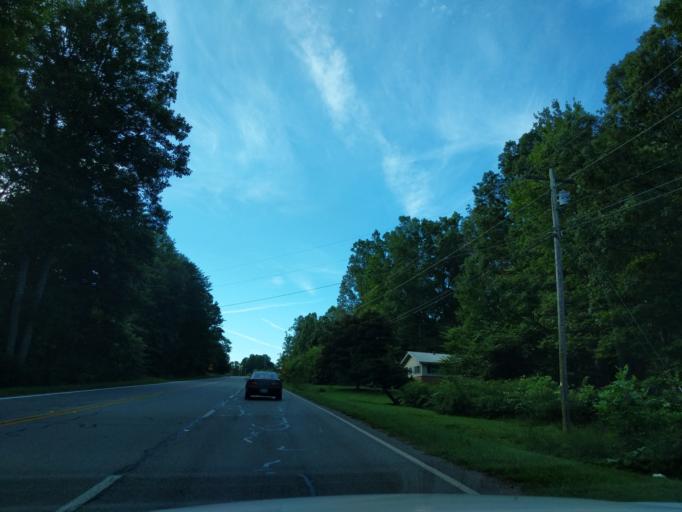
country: US
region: Georgia
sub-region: Fannin County
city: Blue Ridge
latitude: 34.9063
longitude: -84.3760
